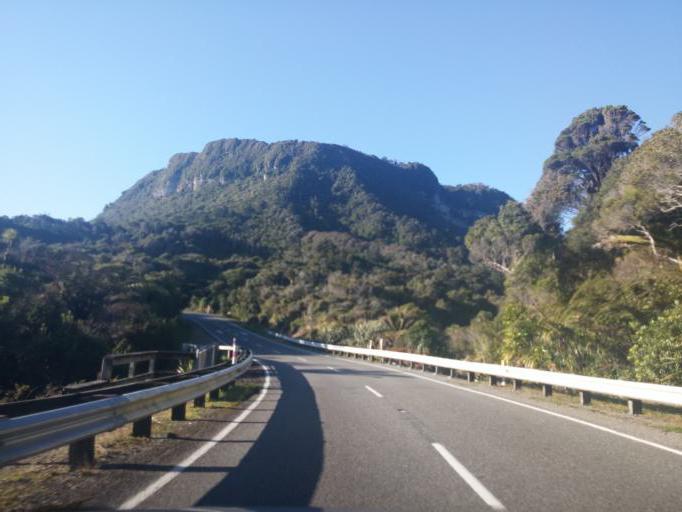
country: NZ
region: West Coast
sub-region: Grey District
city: Greymouth
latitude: -42.1009
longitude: 171.3411
